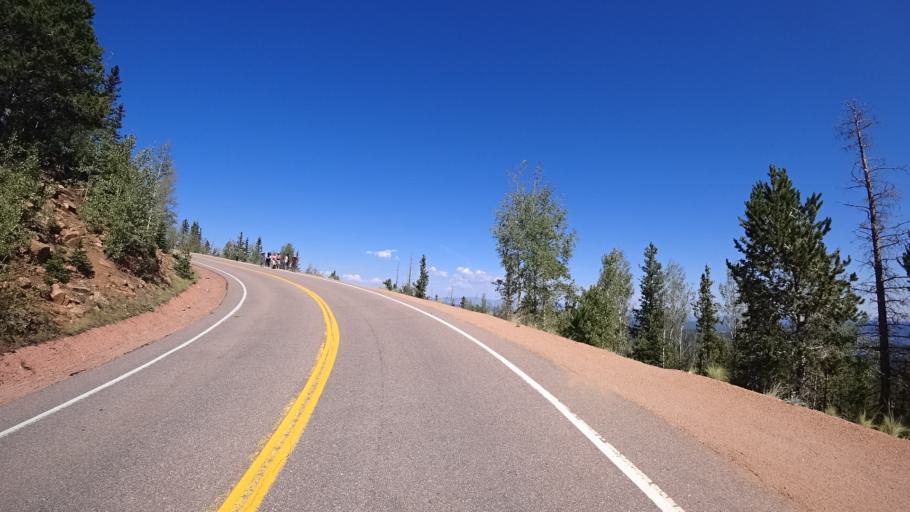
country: US
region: Colorado
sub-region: El Paso County
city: Cascade-Chipita Park
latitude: 38.8936
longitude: -105.0674
